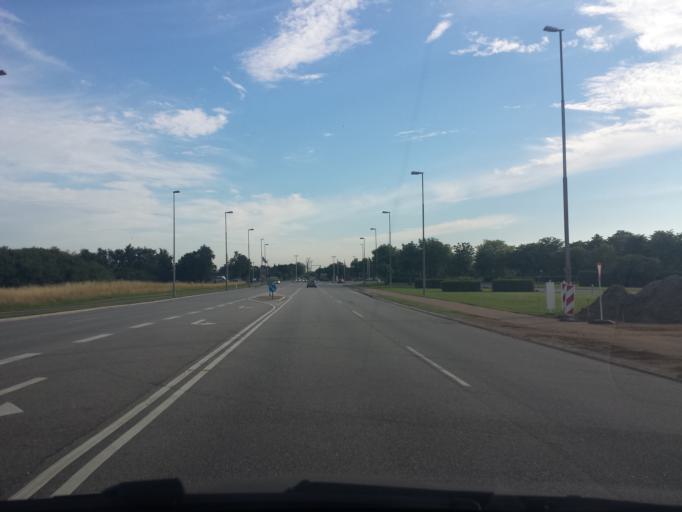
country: DK
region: Capital Region
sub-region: Ballerup Kommune
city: Ballerup
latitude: 55.7341
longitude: 12.3763
